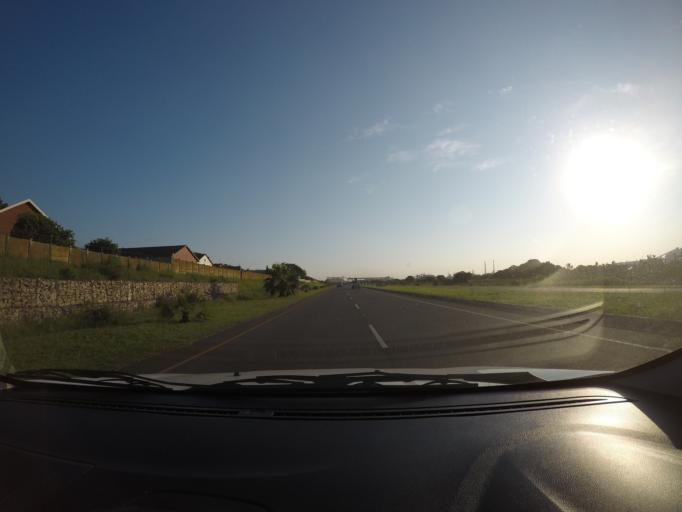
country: ZA
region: KwaZulu-Natal
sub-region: uThungulu District Municipality
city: Richards Bay
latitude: -28.7606
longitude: 32.0514
